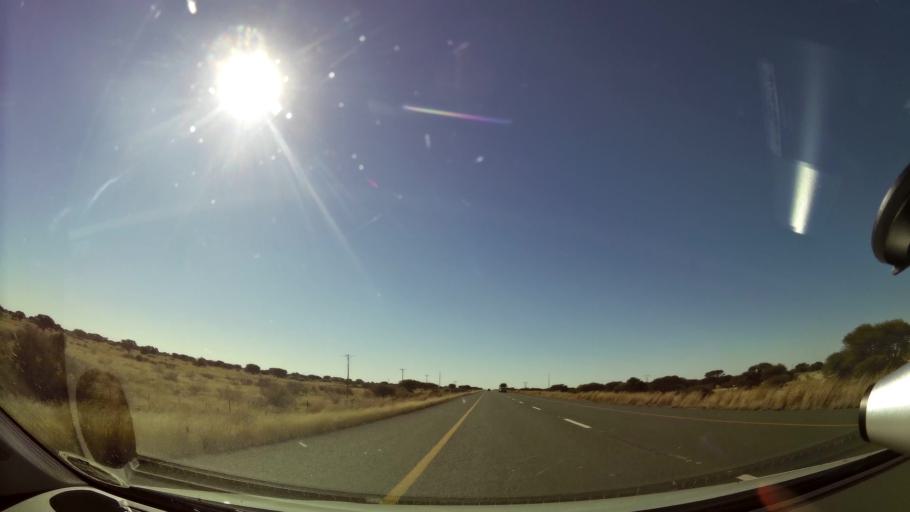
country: ZA
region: Northern Cape
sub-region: Frances Baard District Municipality
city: Warrenton
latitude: -28.0647
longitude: 24.9297
